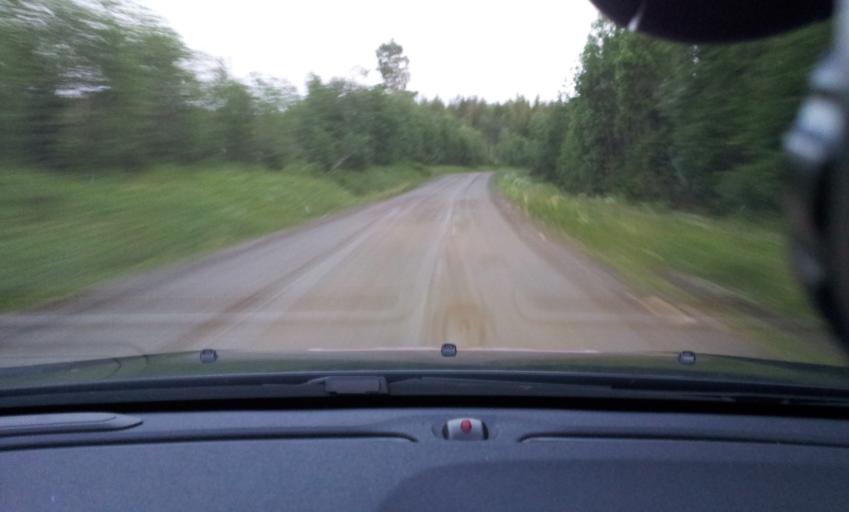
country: SE
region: Jaemtland
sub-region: Ragunda Kommun
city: Hammarstrand
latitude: 62.8727
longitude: 16.0581
